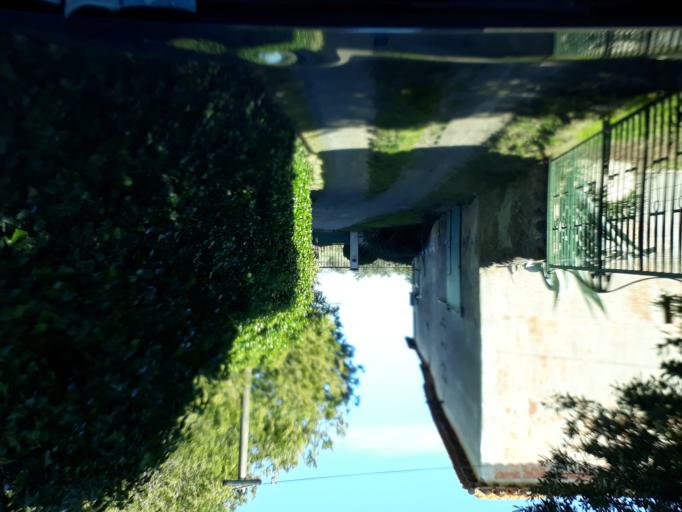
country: FR
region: Languedoc-Roussillon
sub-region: Departement de l'Herault
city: Agde
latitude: 43.3170
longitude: 3.4470
